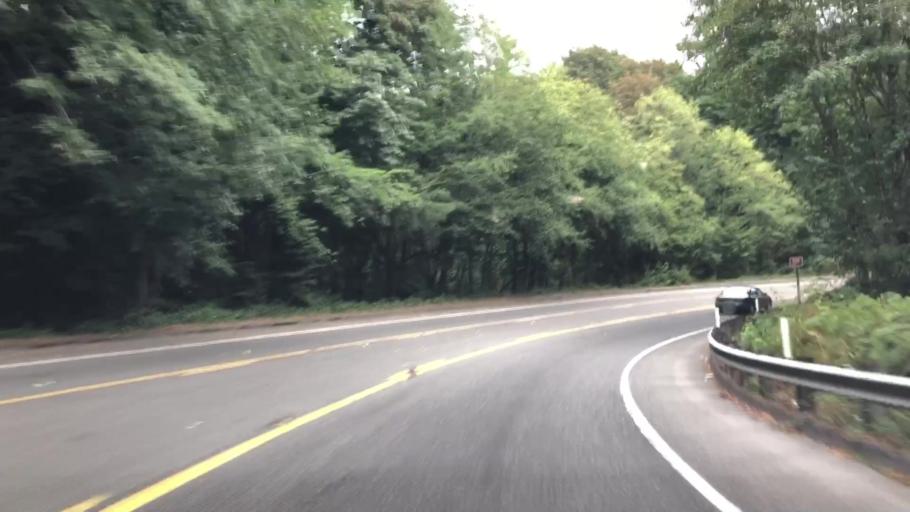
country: US
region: Washington
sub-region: Kitsap County
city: Navy Yard City
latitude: 47.5263
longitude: -122.7055
